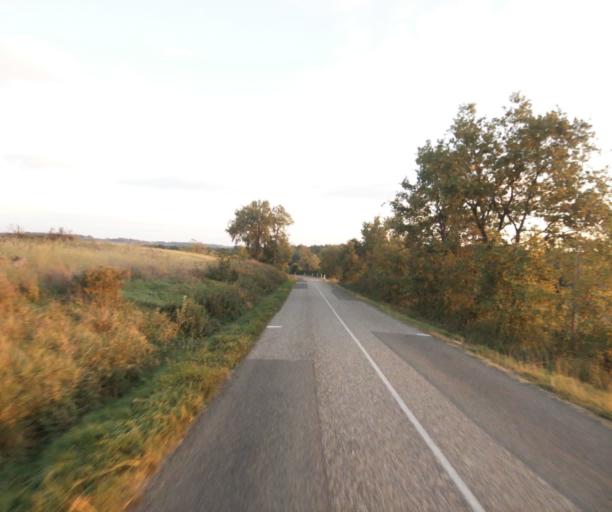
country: FR
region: Midi-Pyrenees
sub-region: Departement du Gers
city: Vic-Fezensac
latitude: 43.7958
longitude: 0.2470
